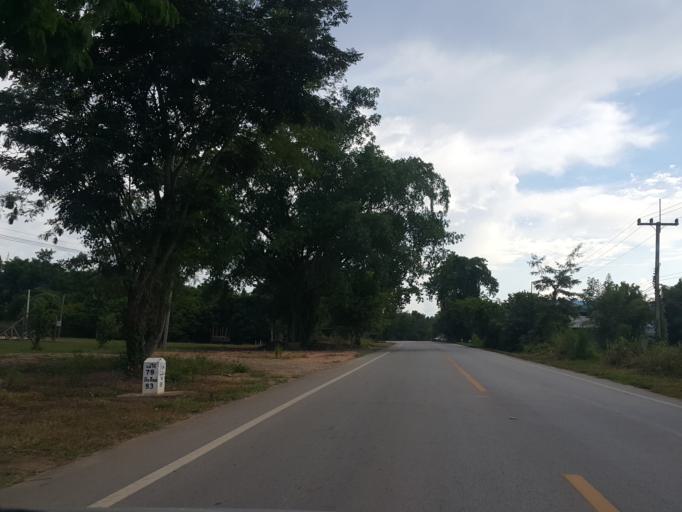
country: TH
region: Chiang Mai
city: Phrao
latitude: 19.3262
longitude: 99.1902
